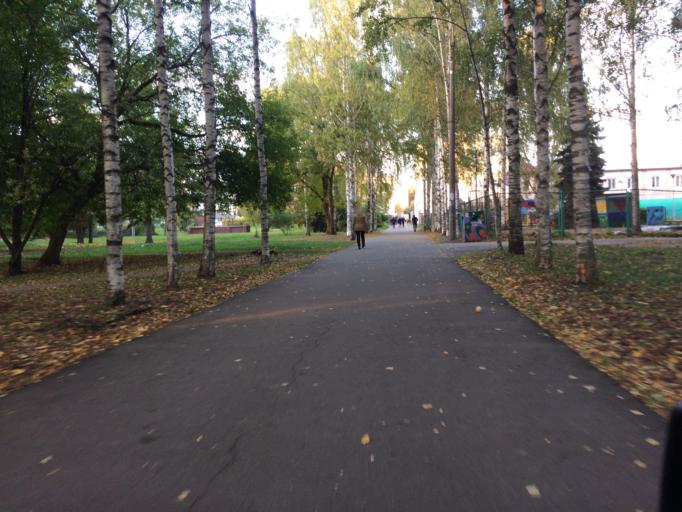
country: RU
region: Mariy-El
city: Yoshkar-Ola
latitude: 56.6371
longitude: 47.8900
